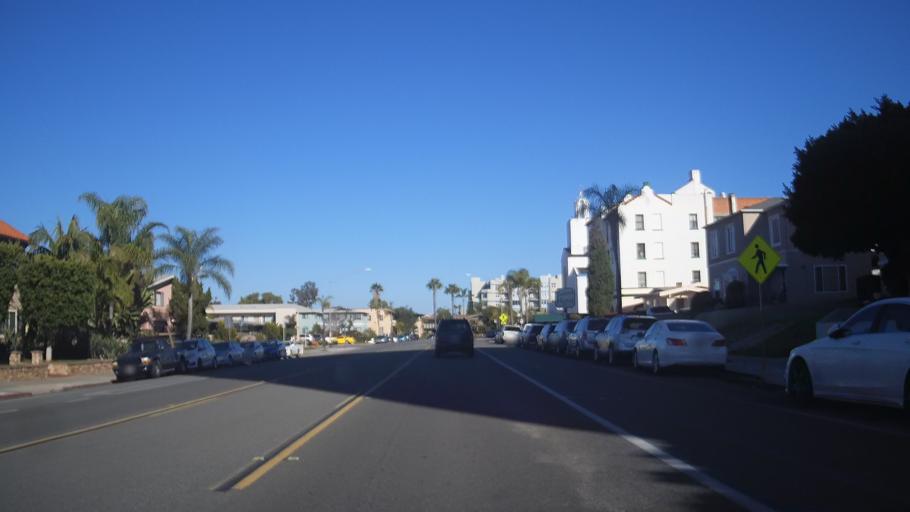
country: US
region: California
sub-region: San Diego County
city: San Diego
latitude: 32.7432
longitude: -117.1475
